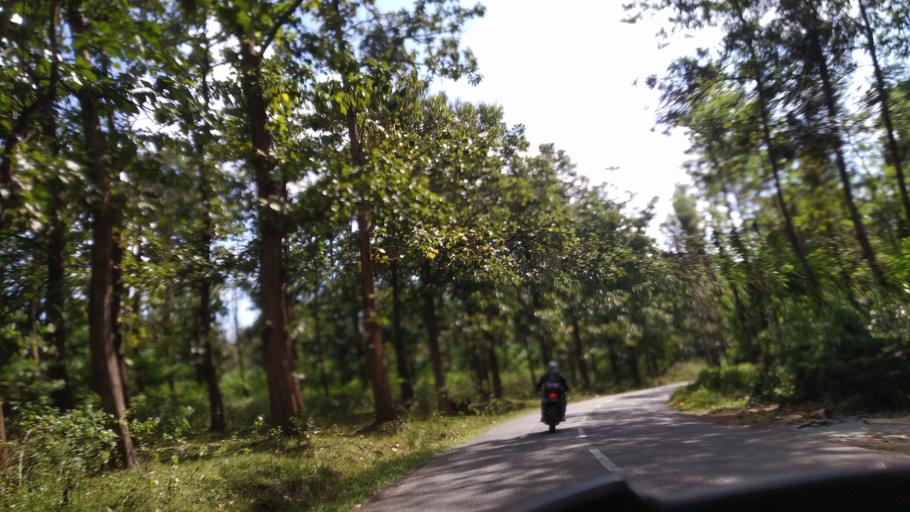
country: IN
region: Kerala
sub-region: Wayanad
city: Panamaram
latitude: 11.9364
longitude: 76.0648
